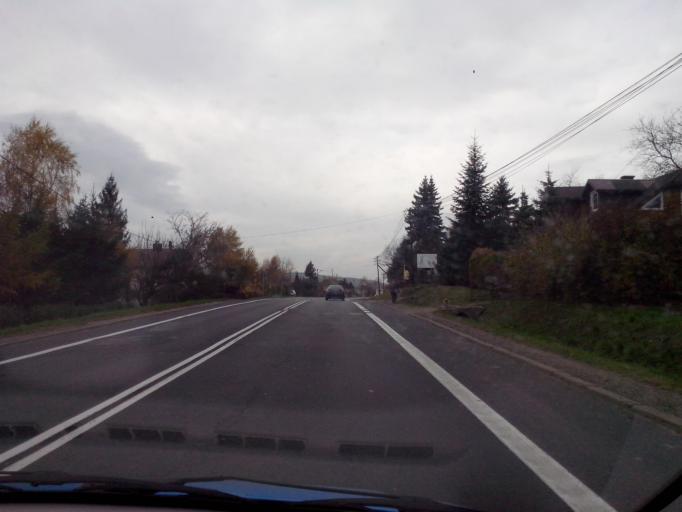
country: PL
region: Subcarpathian Voivodeship
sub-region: Powiat strzyzowski
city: Babica
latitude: 49.9351
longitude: 21.8963
